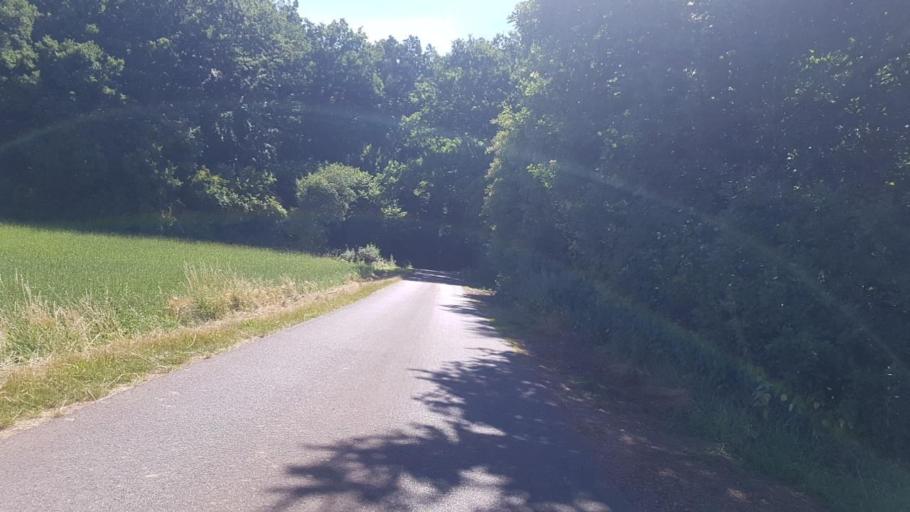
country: DE
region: North Rhine-Westphalia
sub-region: Regierungsbezirk Koln
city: Mechernich
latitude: 50.5973
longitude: 6.6227
